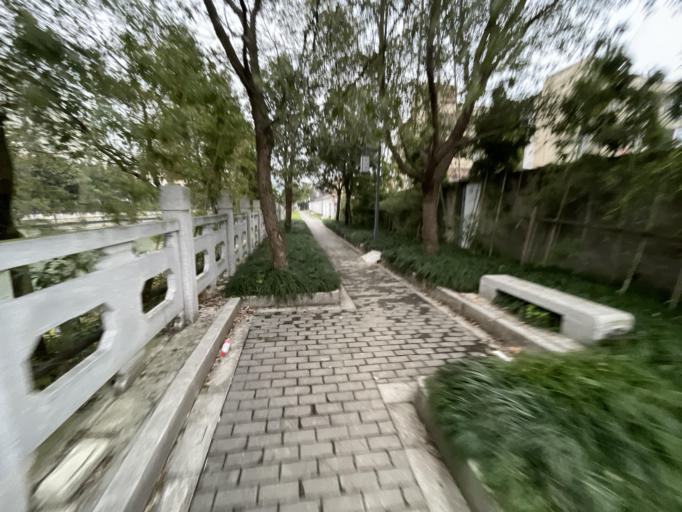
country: CN
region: Zhejiang Sheng
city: Louqiao
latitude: 27.9817
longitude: 120.6194
